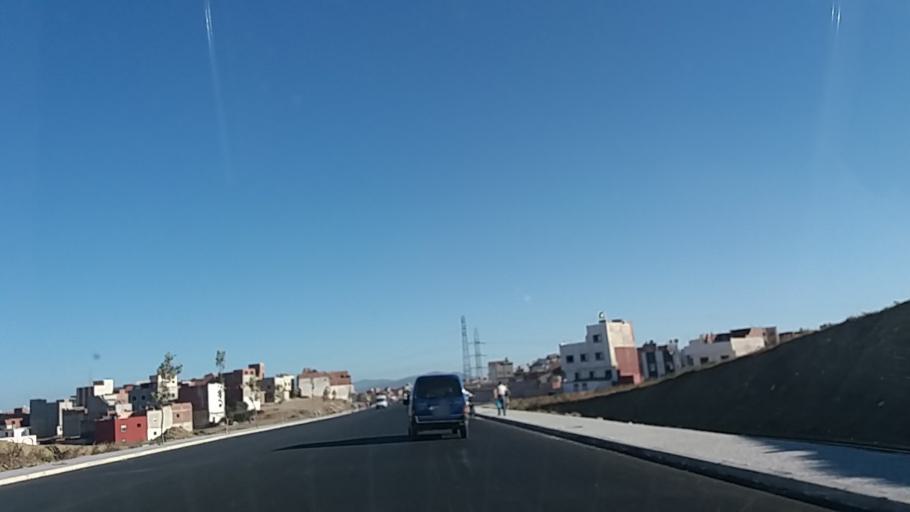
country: MA
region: Tanger-Tetouan
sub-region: Tanger-Assilah
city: Tangier
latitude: 35.7334
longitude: -5.7881
